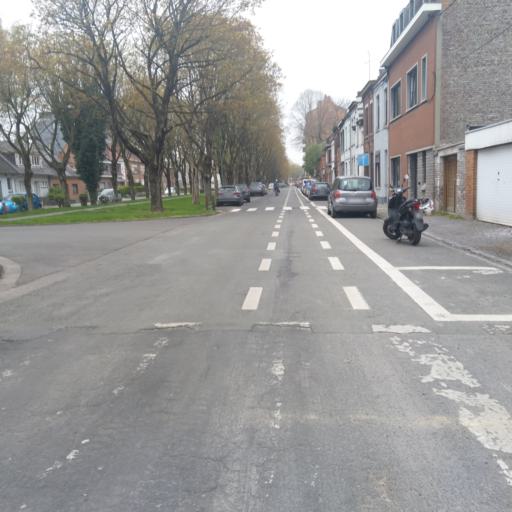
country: BE
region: Wallonia
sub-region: Province du Hainaut
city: Mons
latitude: 50.4459
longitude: 3.9532
